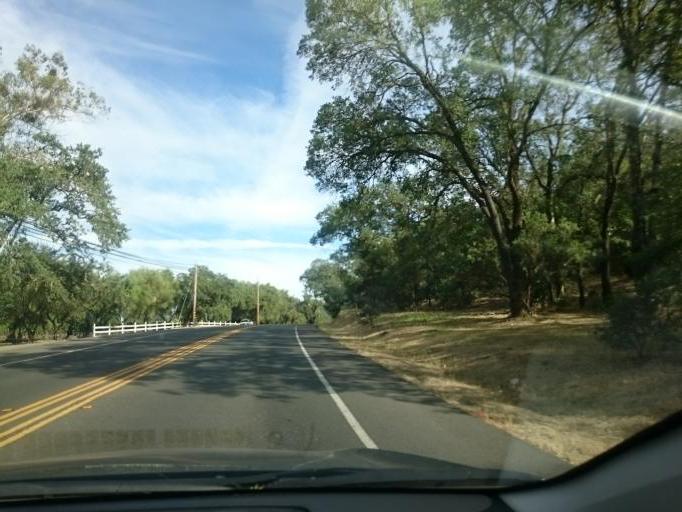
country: US
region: California
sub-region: Napa County
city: Deer Park
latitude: 38.5271
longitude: -122.4989
